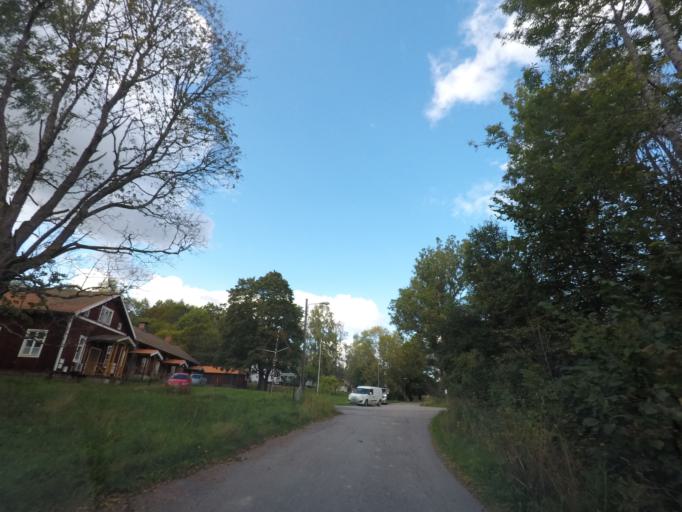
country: SE
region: Vaestmanland
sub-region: Skinnskattebergs Kommun
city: Skinnskatteberg
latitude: 59.8266
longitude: 15.6765
